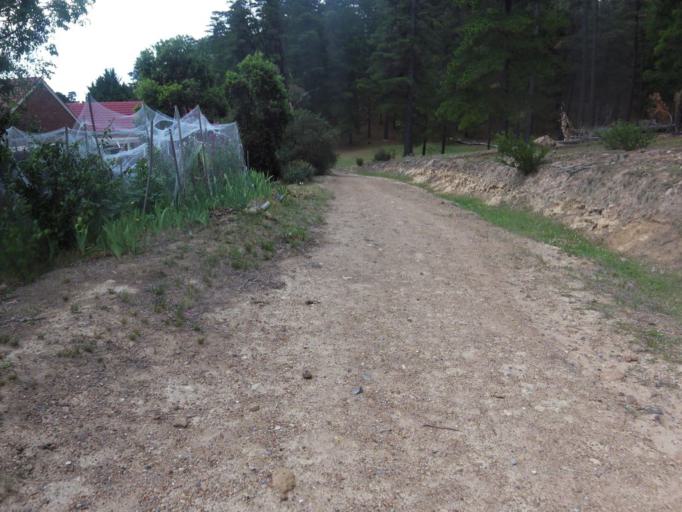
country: AU
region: Australian Capital Territory
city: Macarthur
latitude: -35.3751
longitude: 149.1187
